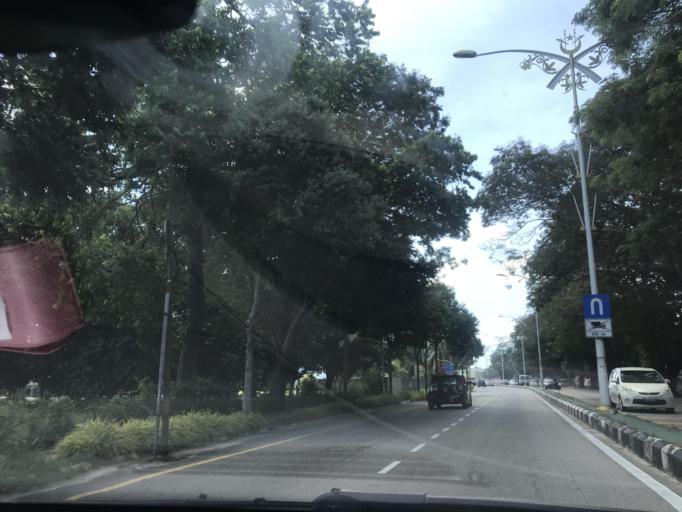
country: MY
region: Kelantan
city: Kota Bharu
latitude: 6.1083
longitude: 102.2506
